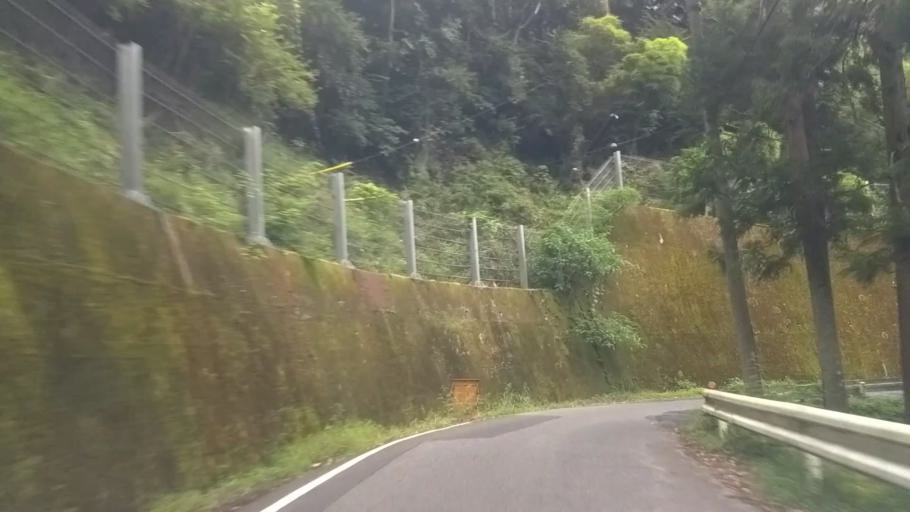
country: JP
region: Chiba
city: Kawaguchi
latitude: 35.1853
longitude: 140.1352
